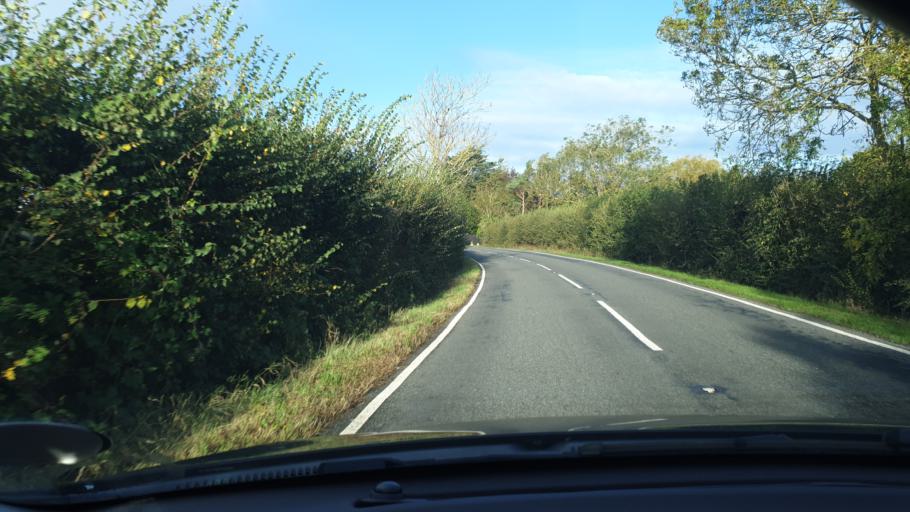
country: GB
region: England
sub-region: Suffolk
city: Shotley Gate
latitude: 51.9355
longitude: 1.2034
